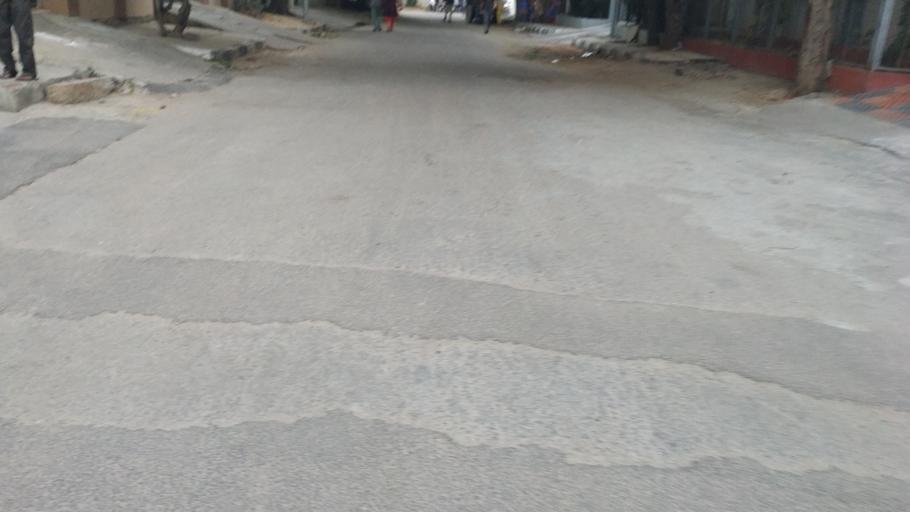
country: IN
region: Telangana
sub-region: Rangareddi
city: Kukatpalli
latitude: 17.4398
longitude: 78.4459
